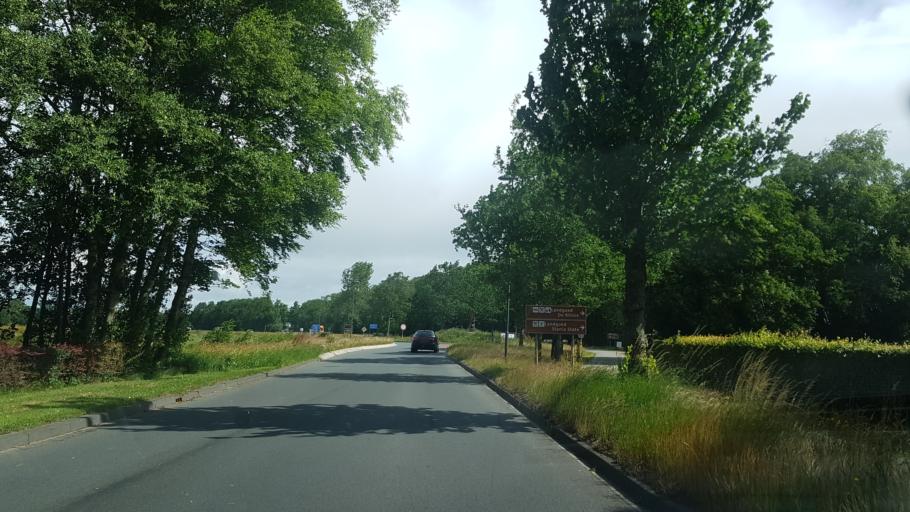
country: NL
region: Friesland
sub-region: Gemeente Tytsjerksteradiel
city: Oentsjerk
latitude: 53.2552
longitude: 5.8961
